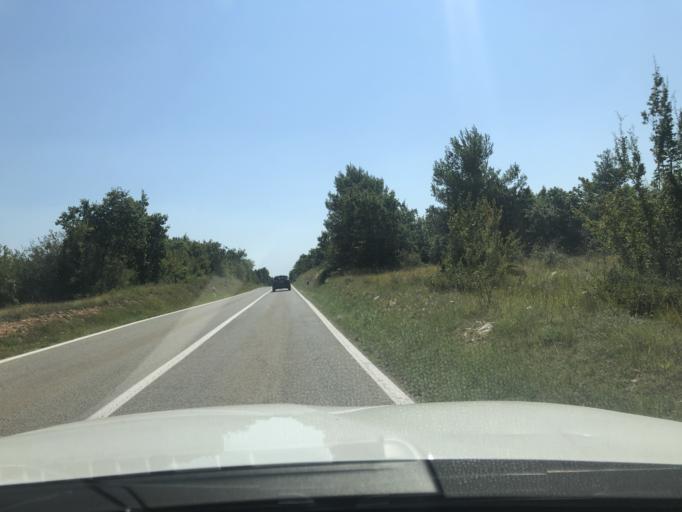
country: HR
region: Istarska
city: Vodnjan
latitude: 45.0140
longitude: 13.8072
